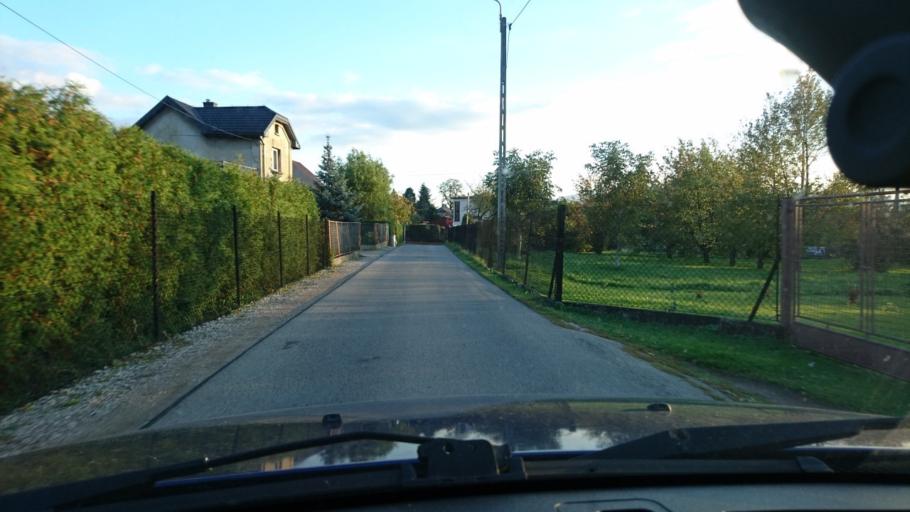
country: PL
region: Silesian Voivodeship
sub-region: Bielsko-Biala
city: Bielsko-Biala
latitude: 49.8409
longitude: 19.0644
